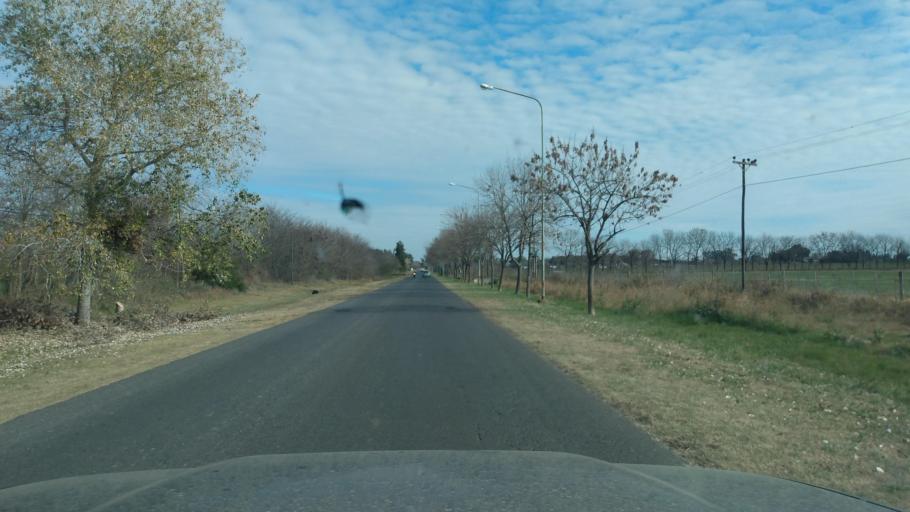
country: AR
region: Buenos Aires
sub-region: Partido de Lujan
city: Lujan
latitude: -34.5756
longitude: -59.1634
